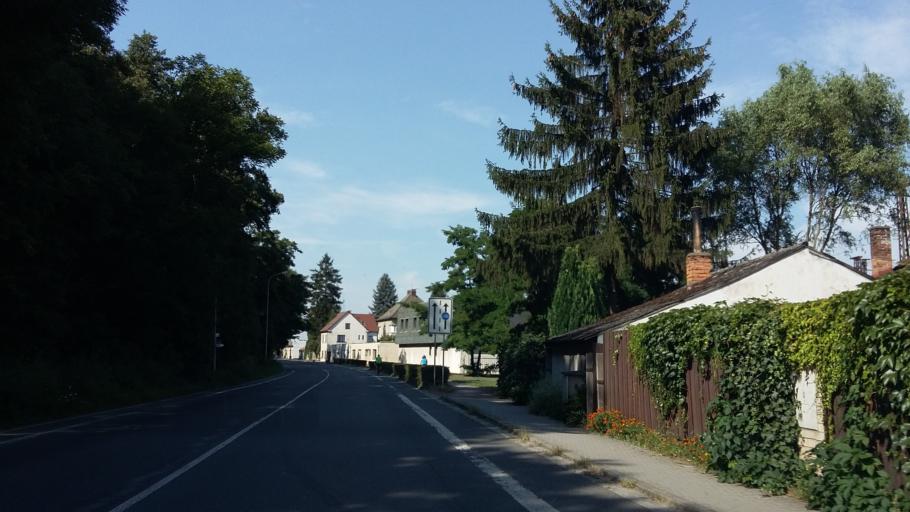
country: CZ
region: Central Bohemia
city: Velky Osek
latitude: 50.1057
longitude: 15.1921
